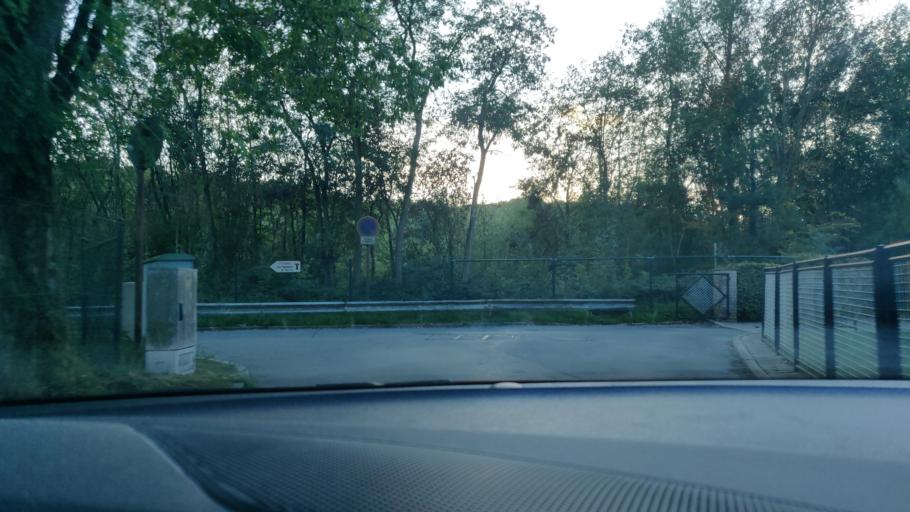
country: DE
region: North Rhine-Westphalia
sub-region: Regierungsbezirk Dusseldorf
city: Velbert
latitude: 51.3125
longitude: 7.0564
